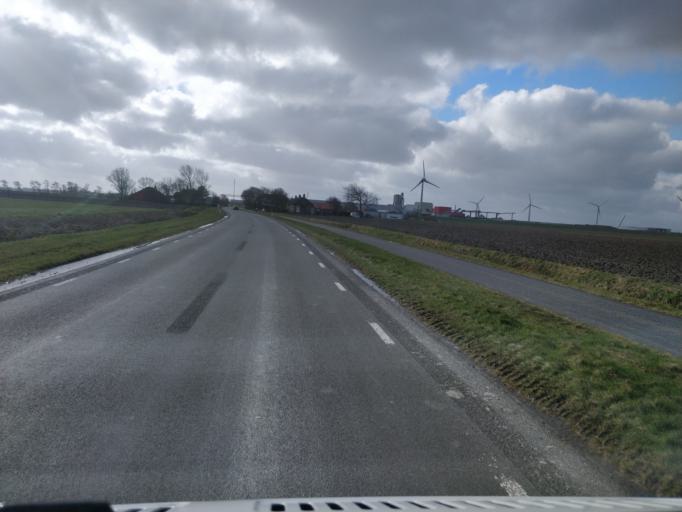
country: NL
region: Friesland
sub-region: Gemeente Harlingen
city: Harlingen
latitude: 53.1998
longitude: 5.4482
